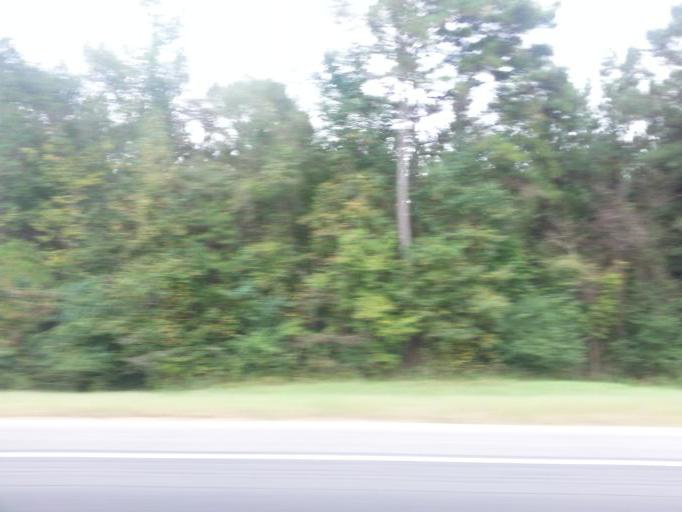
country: US
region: Alabama
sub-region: Butler County
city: Georgiana
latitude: 31.6331
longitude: -86.7932
